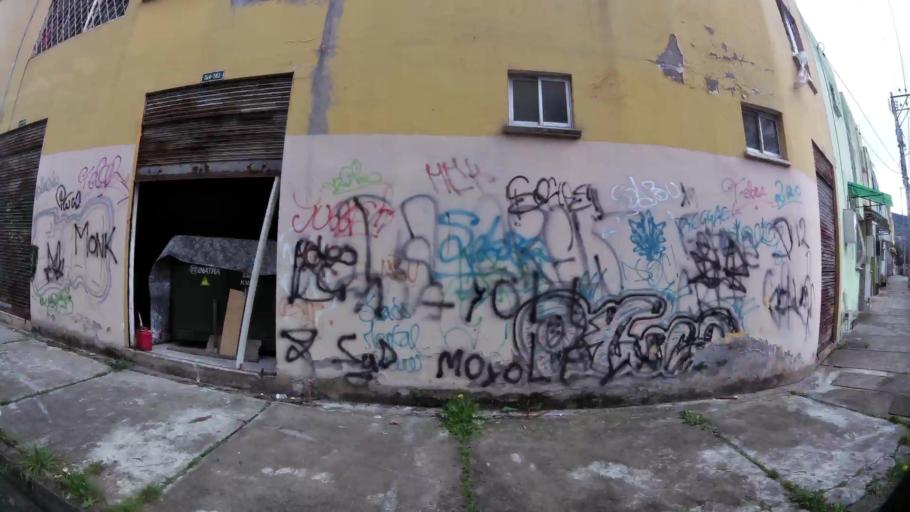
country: EC
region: Pichincha
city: Quito
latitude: -0.2886
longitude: -78.5516
